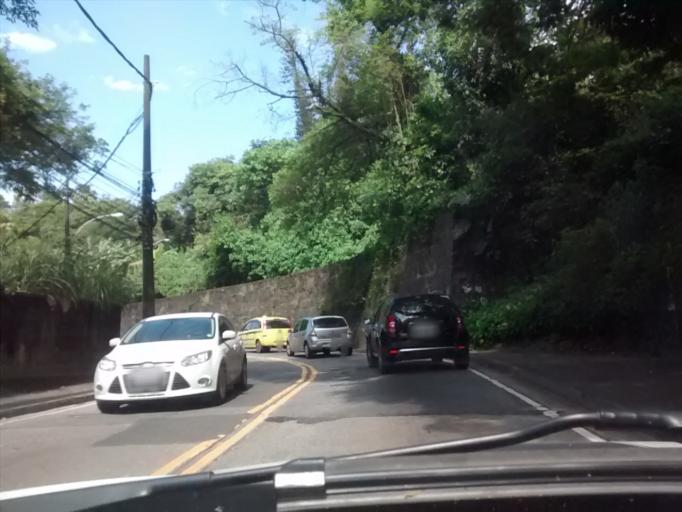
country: BR
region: Rio de Janeiro
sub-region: Rio De Janeiro
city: Rio de Janeiro
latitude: -22.9670
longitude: -43.2782
